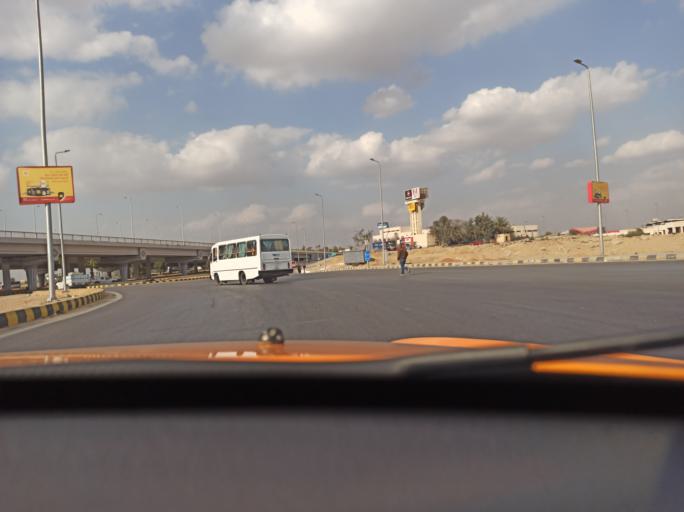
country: EG
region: Eastern Province
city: Bilbays
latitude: 30.2402
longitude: 31.7208
